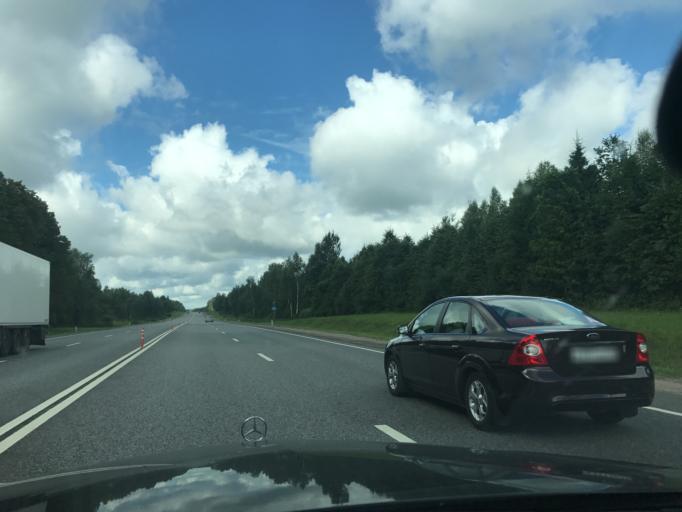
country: RU
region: Smolensk
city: Golynki
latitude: 54.7417
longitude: 31.4002
